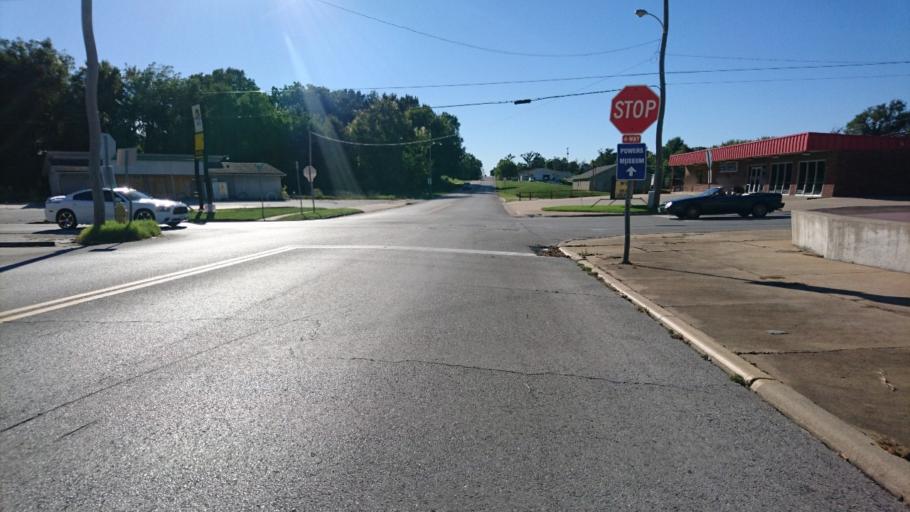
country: US
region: Missouri
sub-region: Jasper County
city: Carthage
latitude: 37.1766
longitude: -94.3271
